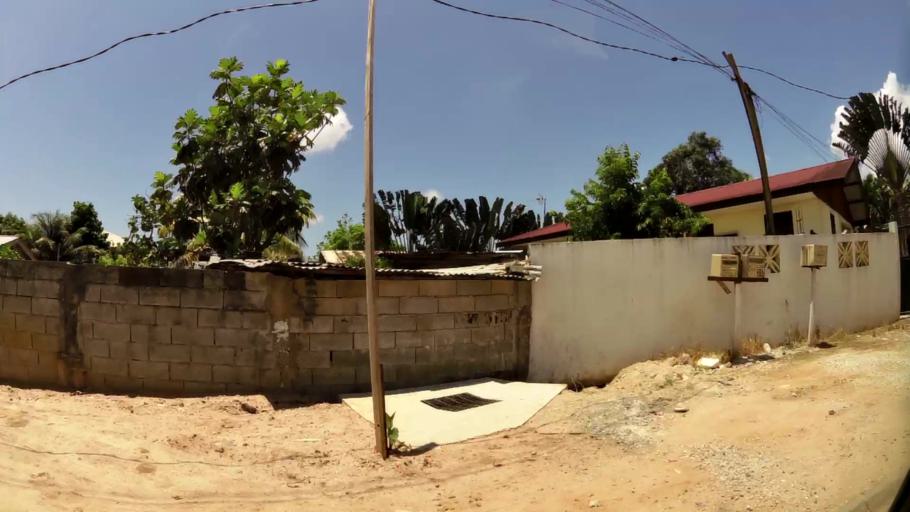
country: GF
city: Macouria
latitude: 4.8851
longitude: -52.3427
